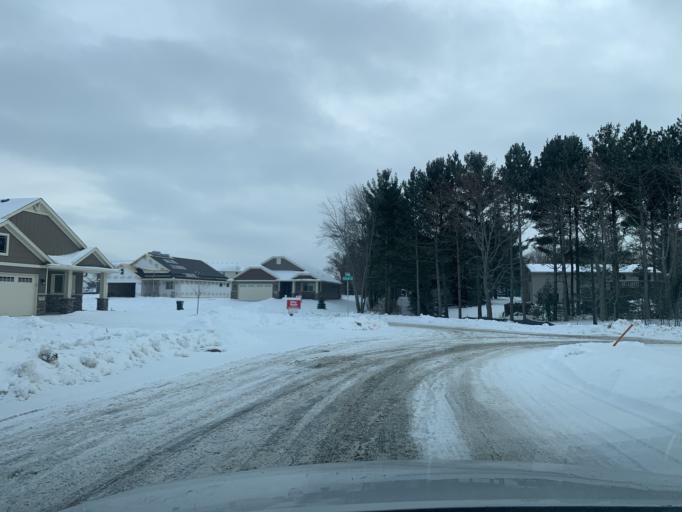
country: US
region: Minnesota
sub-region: Anoka County
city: Ramsey
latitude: 45.2467
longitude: -93.4140
